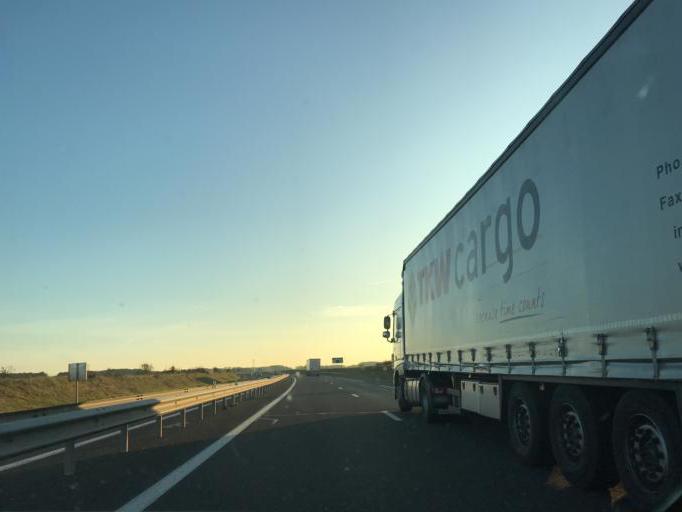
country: FR
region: Bourgogne
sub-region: Departement de l'Yonne
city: Egriselles-le-Bocage
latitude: 48.1853
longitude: 3.1804
